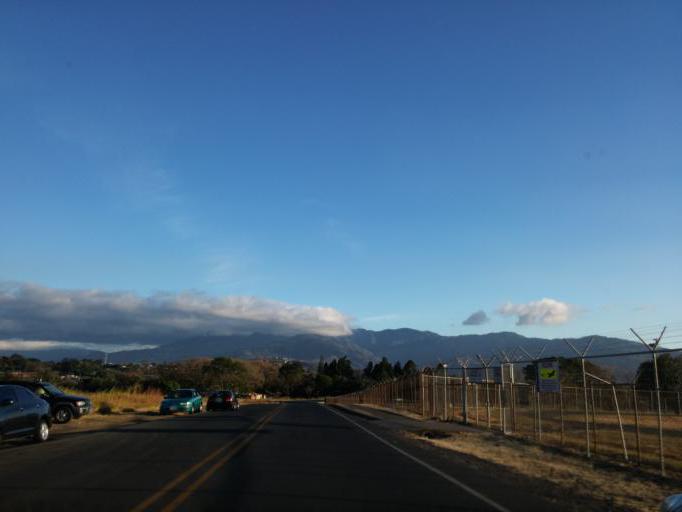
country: CR
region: Heredia
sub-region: Canton de Belen
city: San Antonio
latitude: 9.9986
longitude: -84.1950
